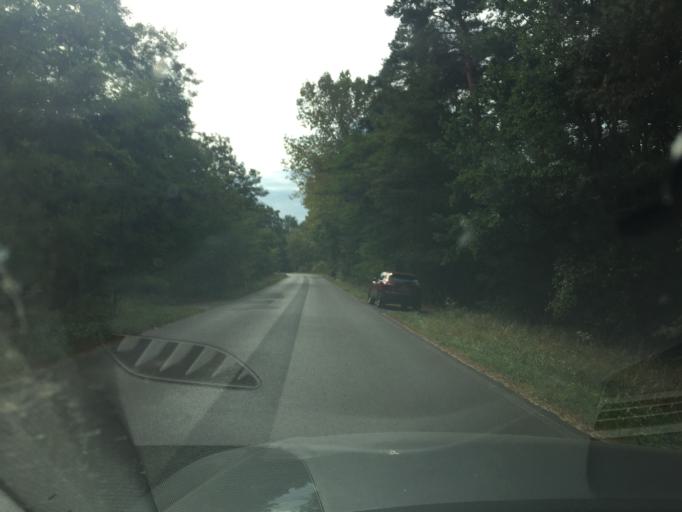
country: DE
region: Brandenburg
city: Erkner
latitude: 52.3941
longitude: 13.7650
